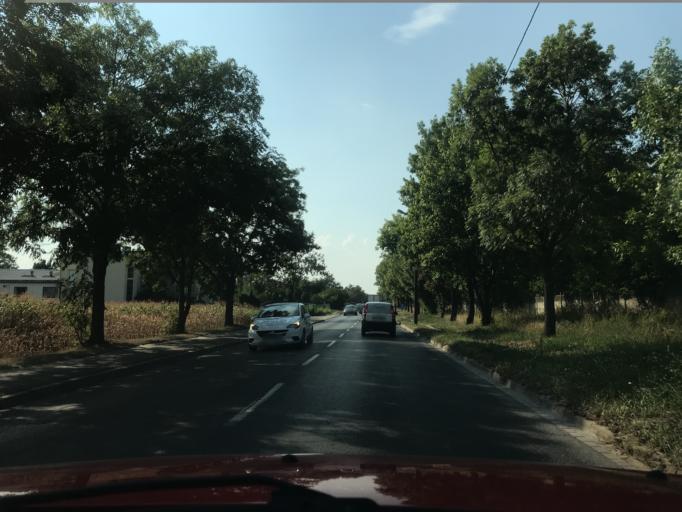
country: PL
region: Greater Poland Voivodeship
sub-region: Powiat poznanski
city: Plewiska
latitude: 52.3724
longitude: 16.8364
